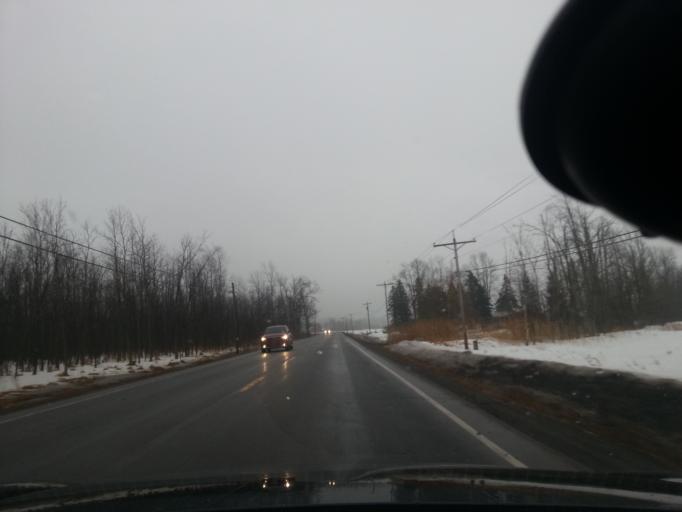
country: US
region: New York
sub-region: St. Lawrence County
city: Ogdensburg
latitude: 44.6302
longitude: -75.4228
